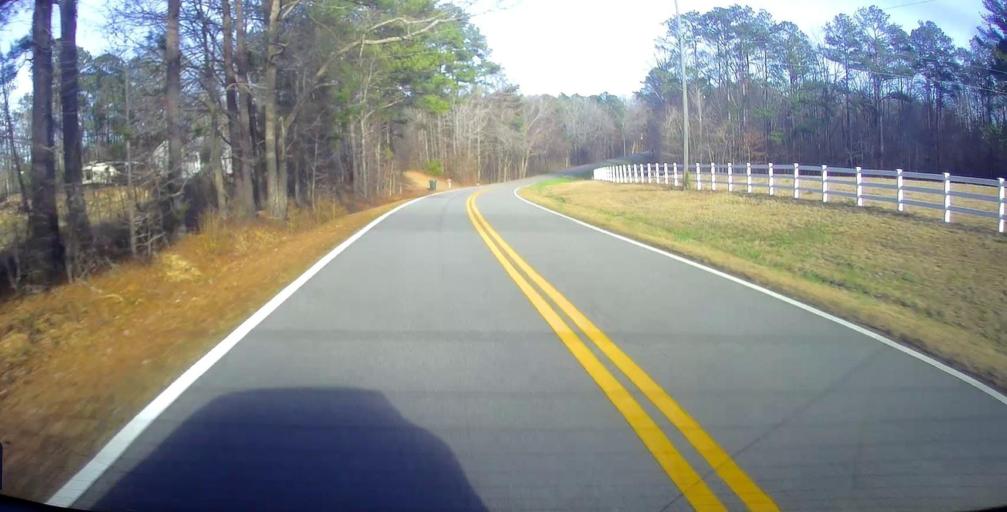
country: US
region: Georgia
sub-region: Bibb County
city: West Point
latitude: 32.8394
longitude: -83.9139
